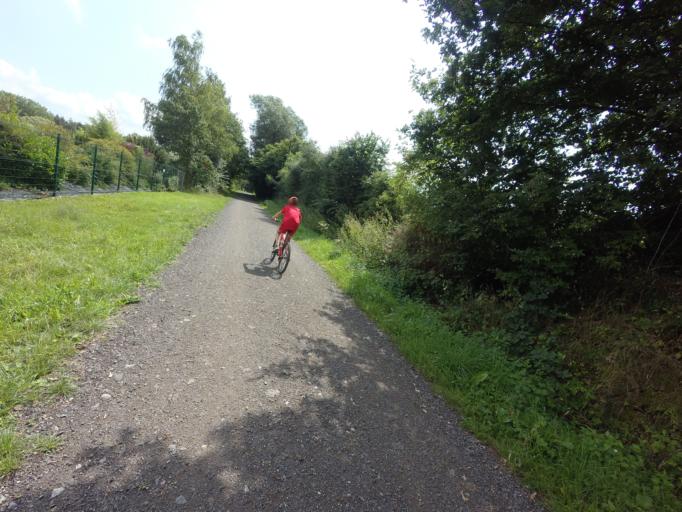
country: BE
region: Wallonia
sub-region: Province de Liege
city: La Calamine
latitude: 50.7162
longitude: 5.9912
